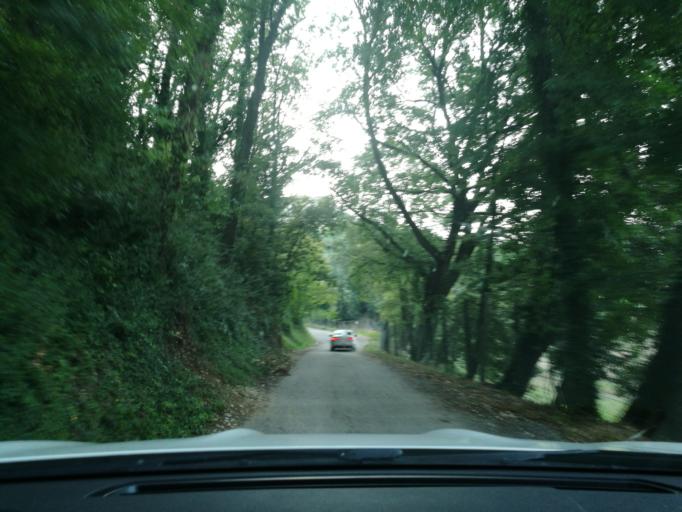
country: IT
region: Umbria
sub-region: Provincia di Terni
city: San Gemini
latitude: 42.6138
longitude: 12.5513
